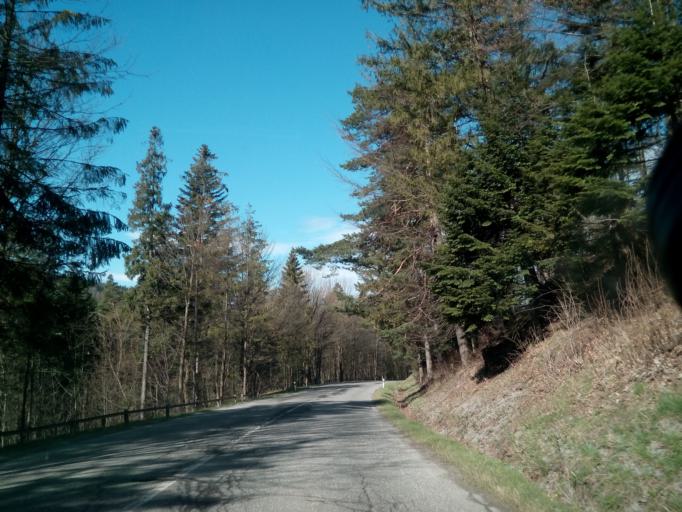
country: SK
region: Presovsky
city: Spisska Bela
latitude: 49.2917
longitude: 20.4146
